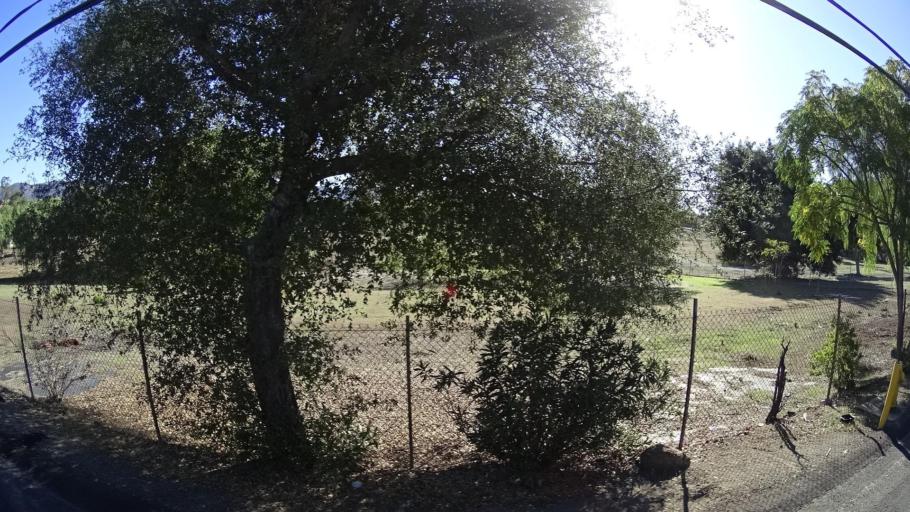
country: US
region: California
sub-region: San Diego County
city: Jamul
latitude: 32.7153
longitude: -116.8761
